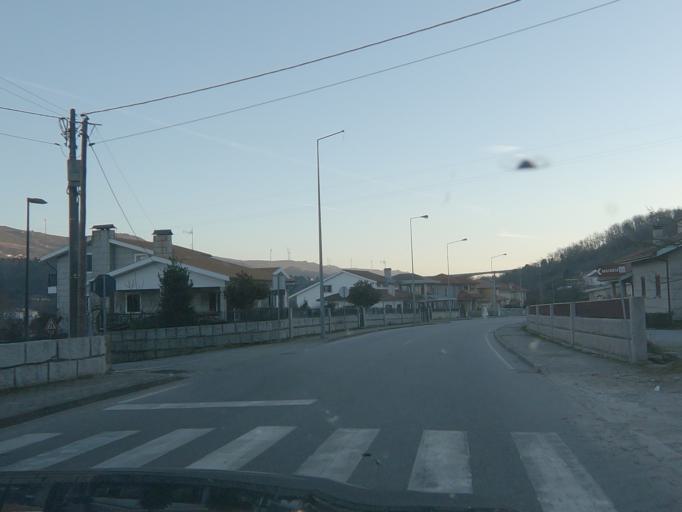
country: PT
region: Vila Real
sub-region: Vila Pouca de Aguiar
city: Vila Pouca de Aguiar
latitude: 41.4965
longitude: -7.6491
